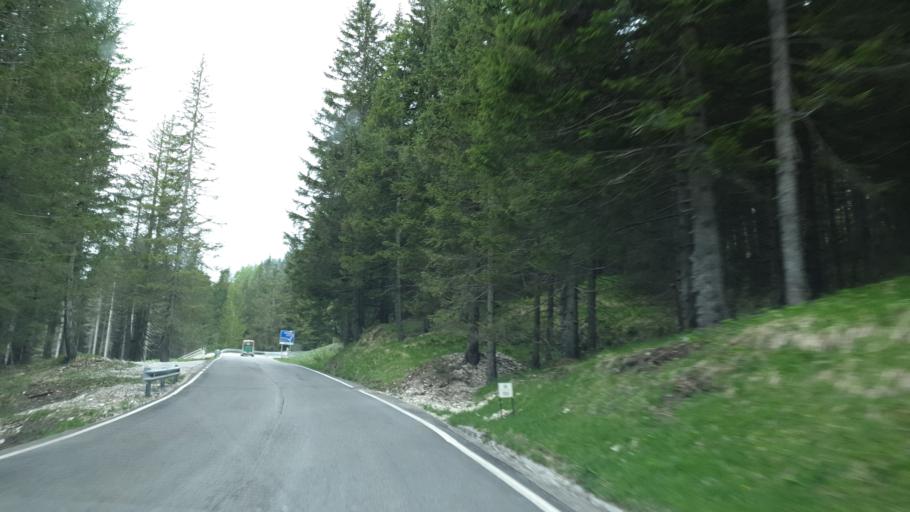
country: IT
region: Veneto
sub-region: Provincia di Belluno
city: San Vito
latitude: 46.5643
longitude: 12.2456
